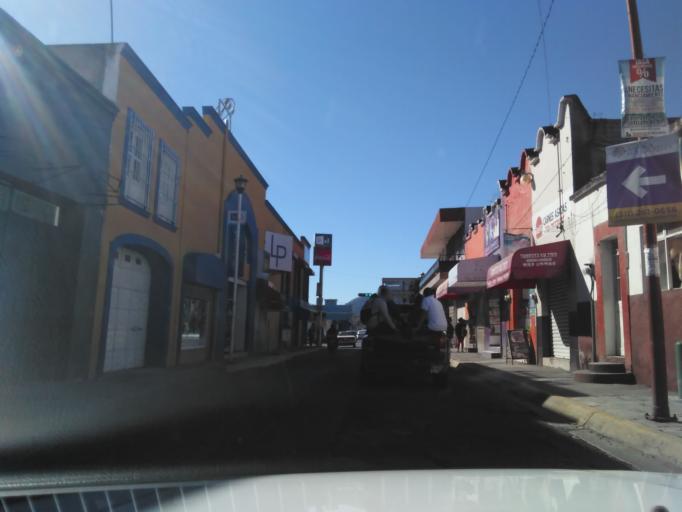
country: MX
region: Nayarit
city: Xalisco
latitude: 21.4451
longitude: -104.8998
